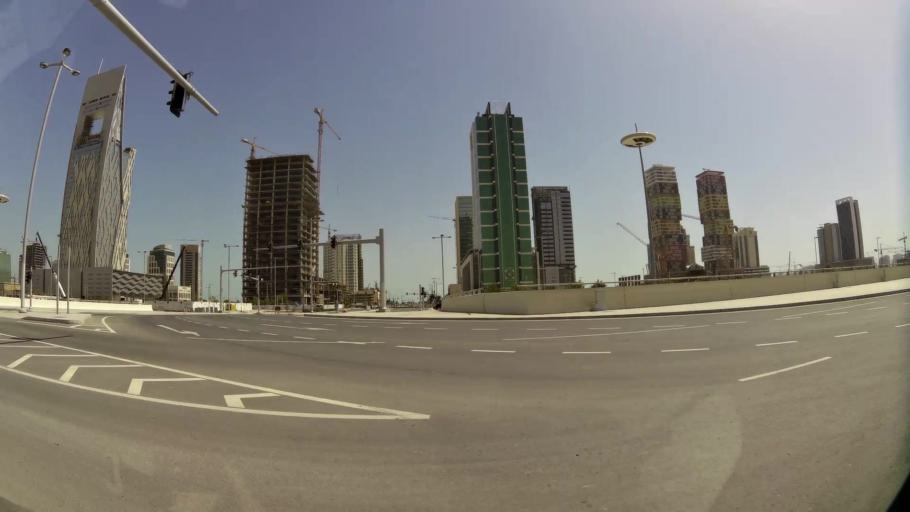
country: QA
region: Baladiyat ad Dawhah
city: Doha
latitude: 25.3885
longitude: 51.5182
